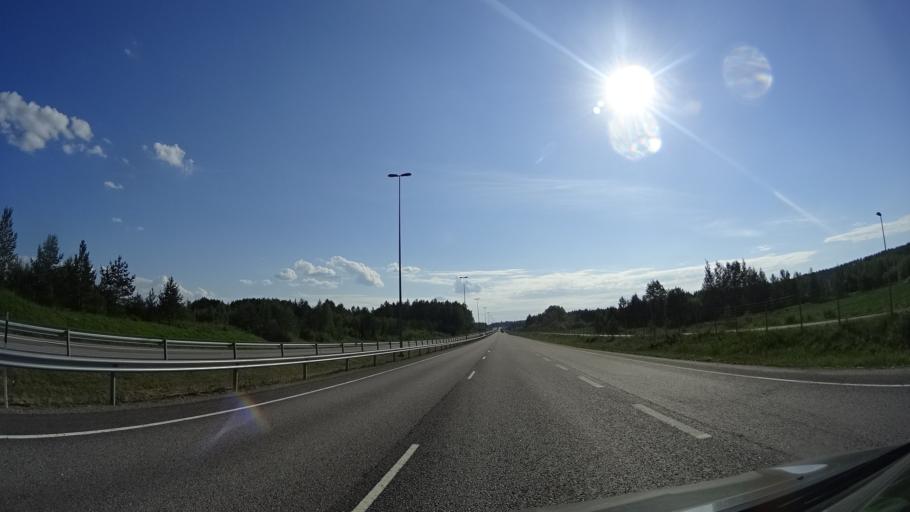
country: FI
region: South Karelia
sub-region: Imatra
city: Imatra
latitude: 61.1829
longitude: 28.7352
